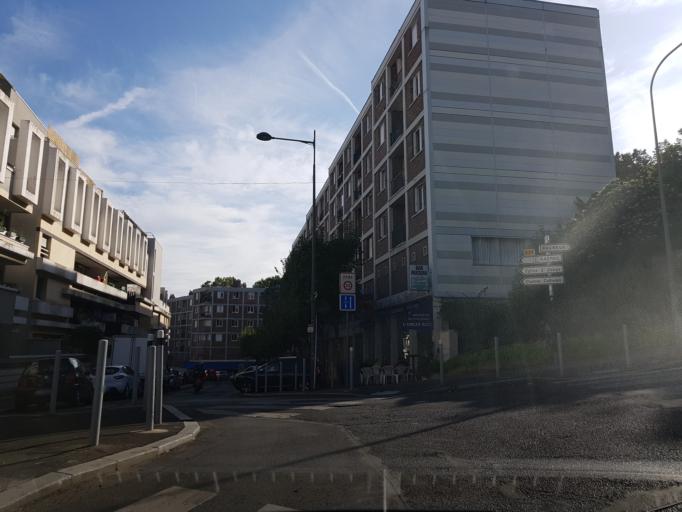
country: FR
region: Ile-de-France
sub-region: Departement du Val-de-Marne
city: Arcueil
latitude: 48.8035
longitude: 2.3322
